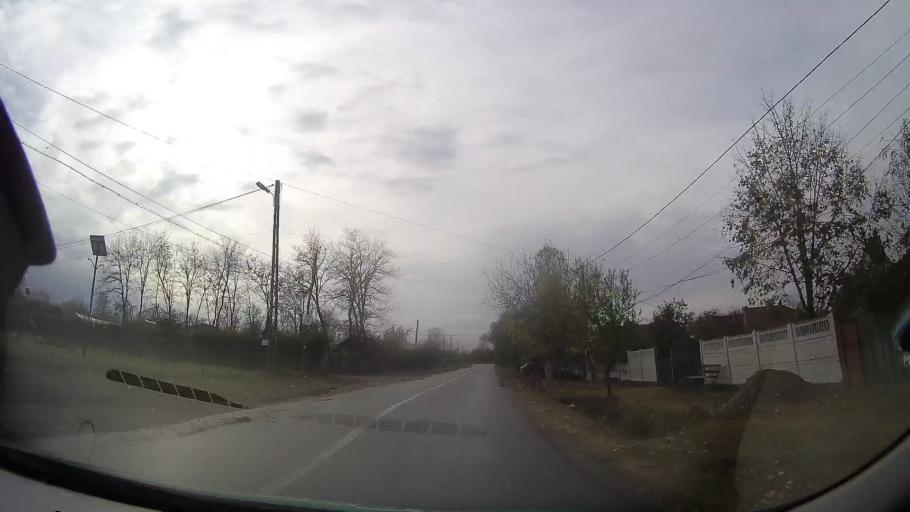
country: RO
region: Ialomita
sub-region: Comuna Maia
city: Maia
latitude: 44.7327
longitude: 26.4006
